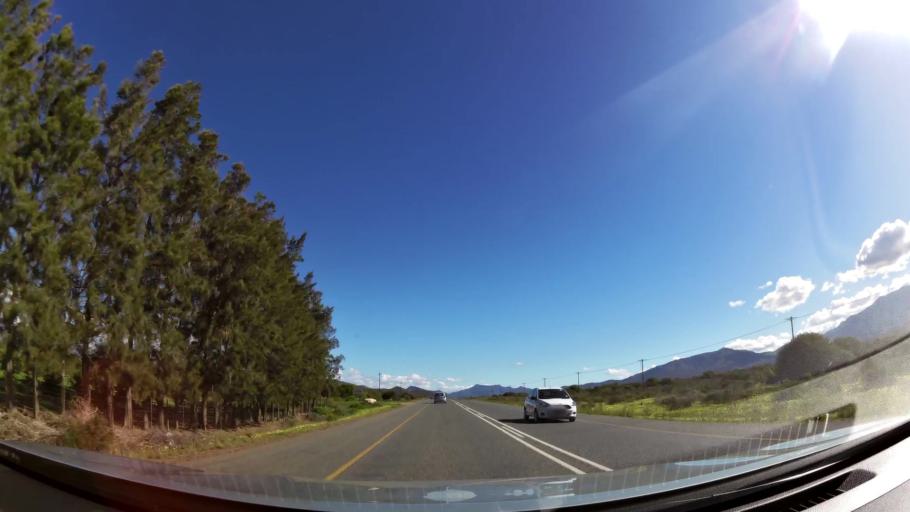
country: ZA
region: Western Cape
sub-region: Cape Winelands District Municipality
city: Ashton
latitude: -33.8145
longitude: 19.9228
